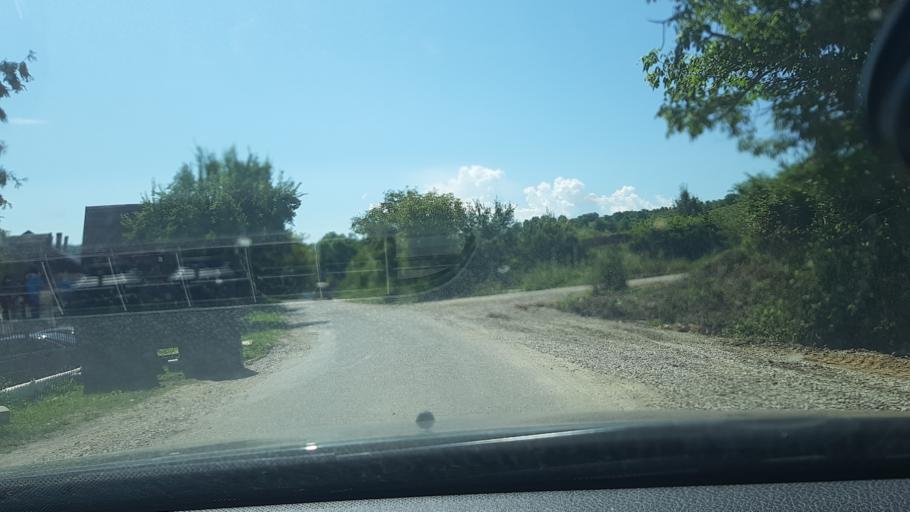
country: RO
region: Hunedoara
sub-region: Comuna Teliucu Inferior
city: Teliucu Inferior
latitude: 45.6859
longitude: 22.8706
